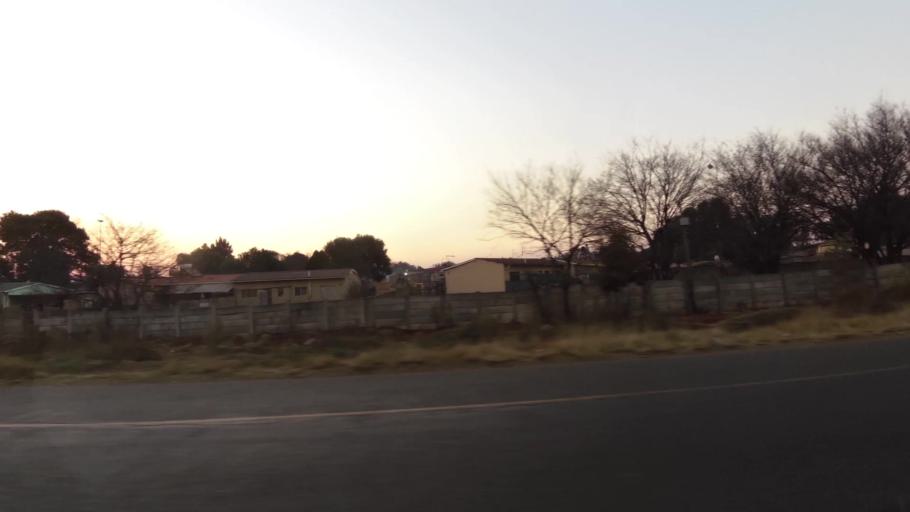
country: ZA
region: Gauteng
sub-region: City of Johannesburg Metropolitan Municipality
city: Soweto
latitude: -26.2922
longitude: 27.8797
